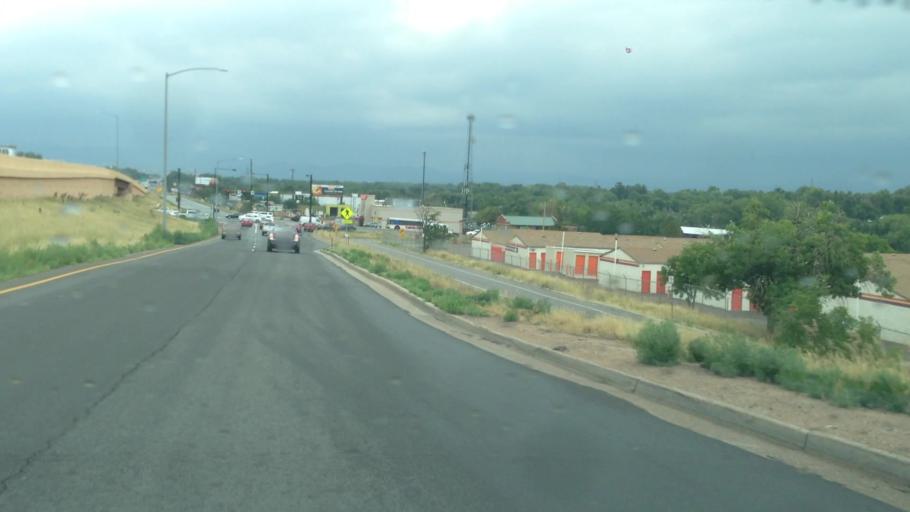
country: US
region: Colorado
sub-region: Jefferson County
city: Edgewater
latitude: 39.7260
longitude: -105.0508
